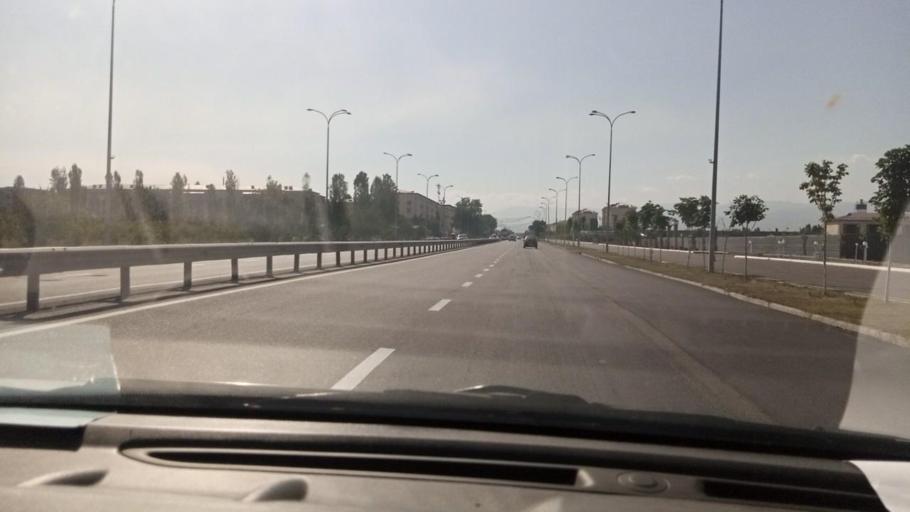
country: UZ
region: Toshkent
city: Ohangaron
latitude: 40.9113
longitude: 69.6181
